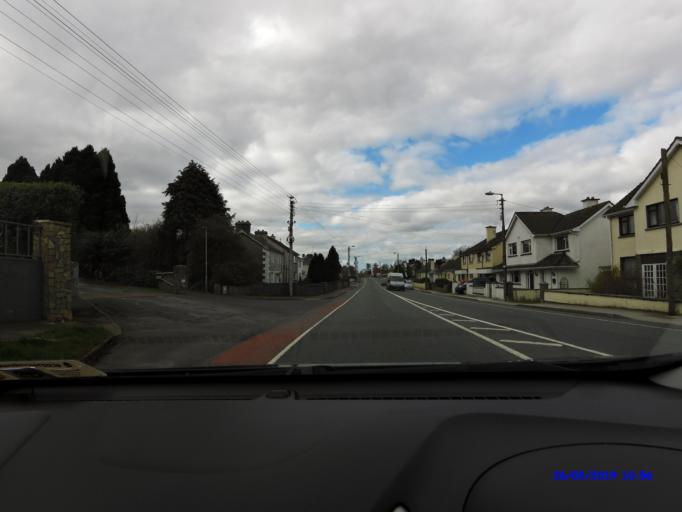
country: IE
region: Connaught
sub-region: Maigh Eo
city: Castlebar
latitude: 53.8579
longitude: -9.3113
